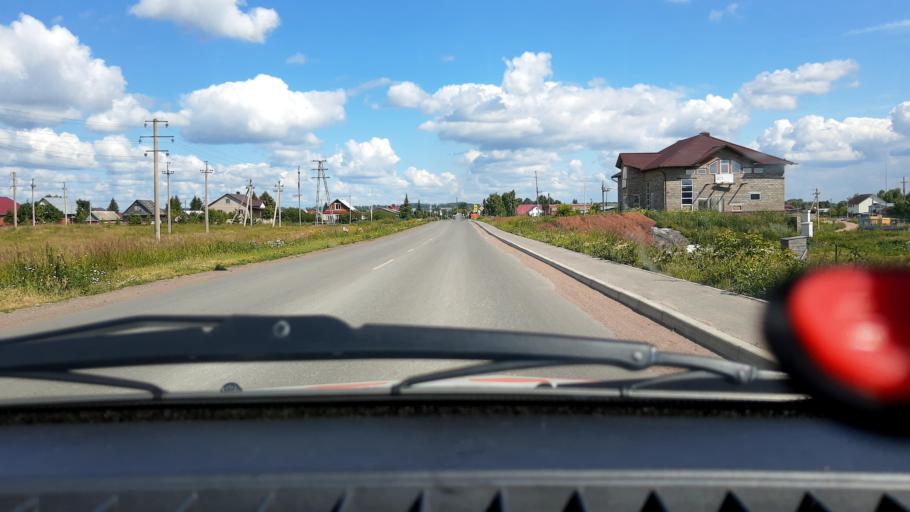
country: RU
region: Bashkortostan
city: Avdon
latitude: 54.4896
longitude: 55.8856
